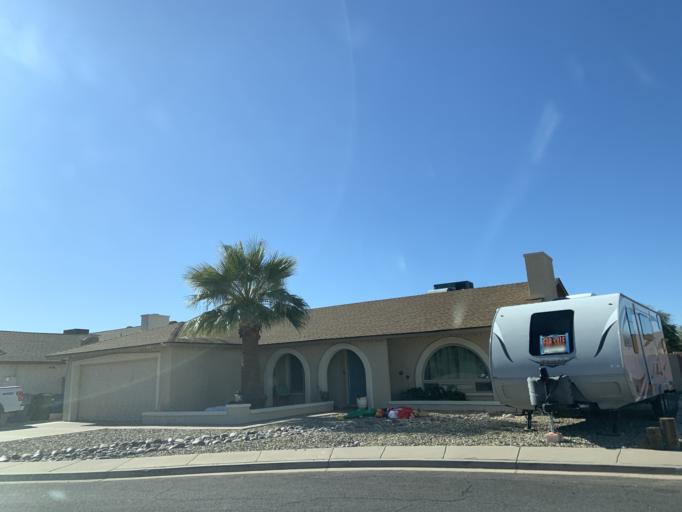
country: US
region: Arizona
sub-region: Maricopa County
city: San Carlos
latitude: 33.3615
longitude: -111.8575
